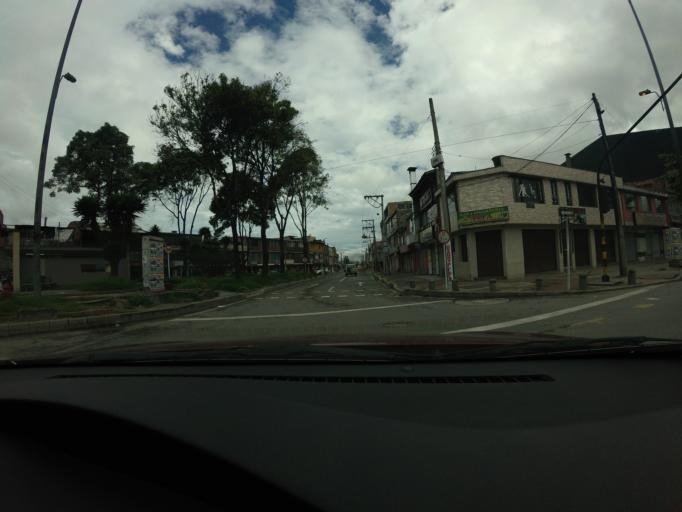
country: CO
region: Bogota D.C.
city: Bogota
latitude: 4.5992
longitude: -74.1450
